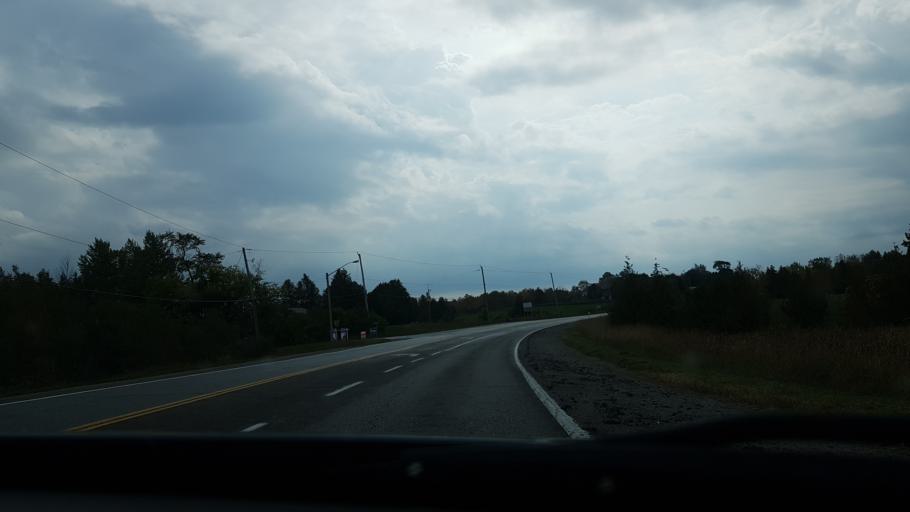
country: CA
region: Ontario
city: Omemee
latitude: 44.4909
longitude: -78.7458
